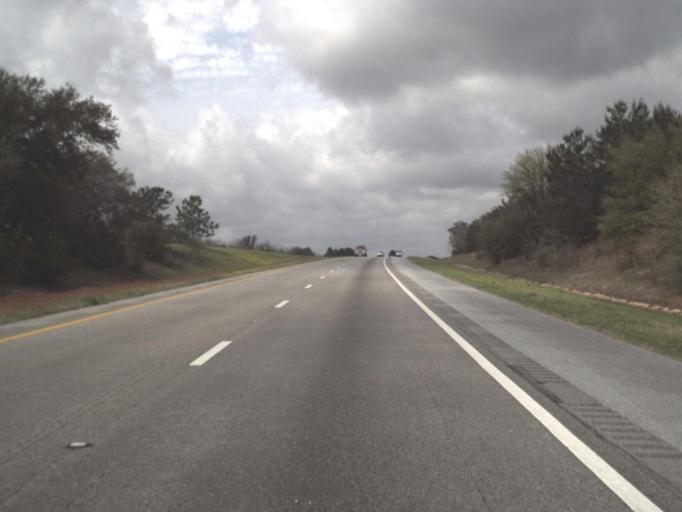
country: US
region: Florida
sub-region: Okaloosa County
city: Crestview
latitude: 30.7179
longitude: -86.4450
